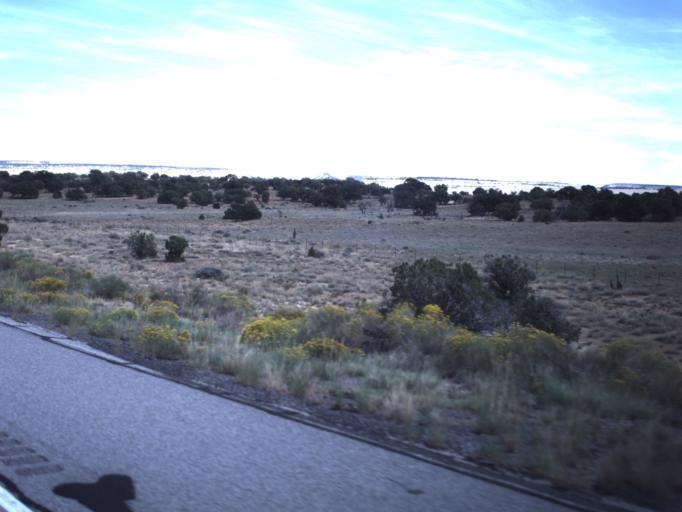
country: US
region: Utah
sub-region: Emery County
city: Castle Dale
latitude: 38.8676
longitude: -110.7037
